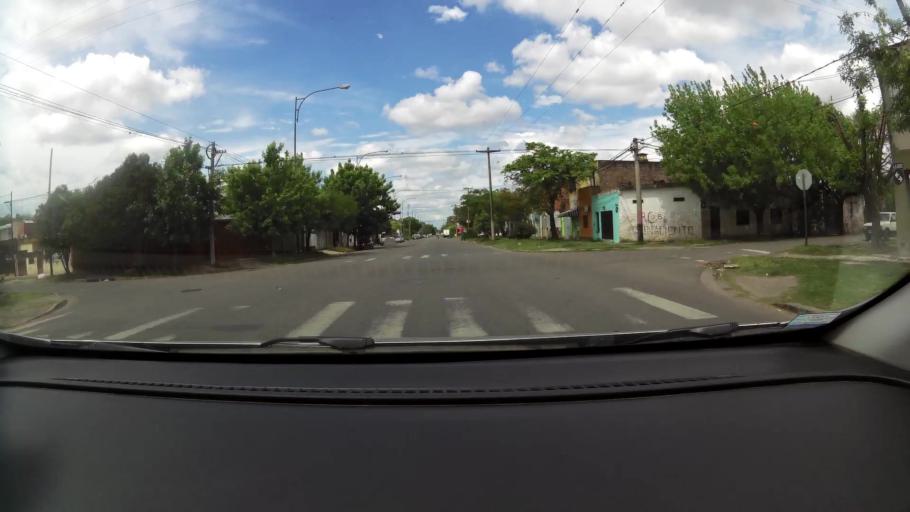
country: AR
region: Santa Fe
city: Gobernador Galvez
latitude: -33.0087
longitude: -60.6400
